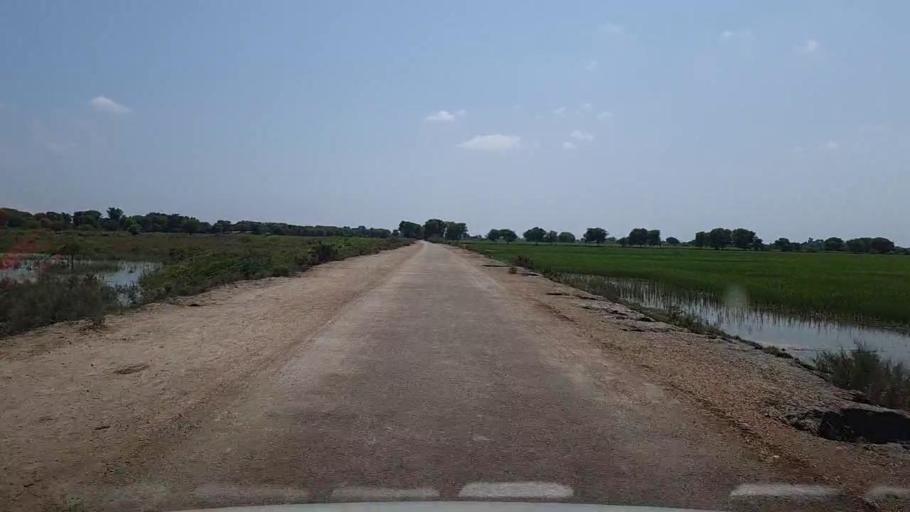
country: PK
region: Sindh
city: Kario
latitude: 24.8294
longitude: 68.7029
